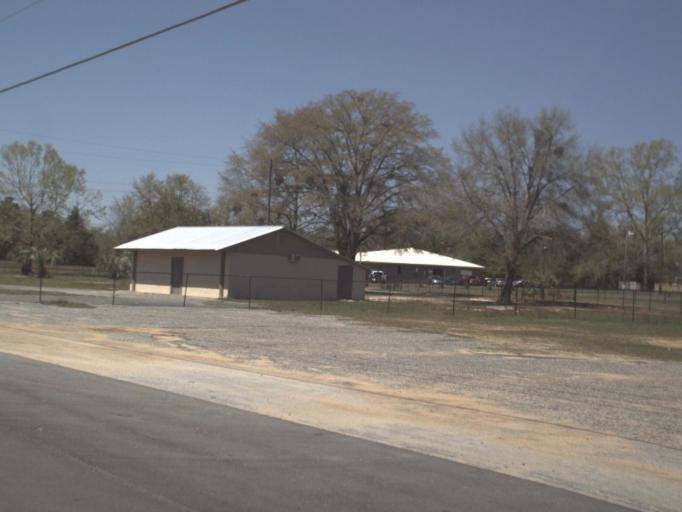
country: US
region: Florida
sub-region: Walton County
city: DeFuniak Springs
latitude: 30.7261
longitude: -86.0935
